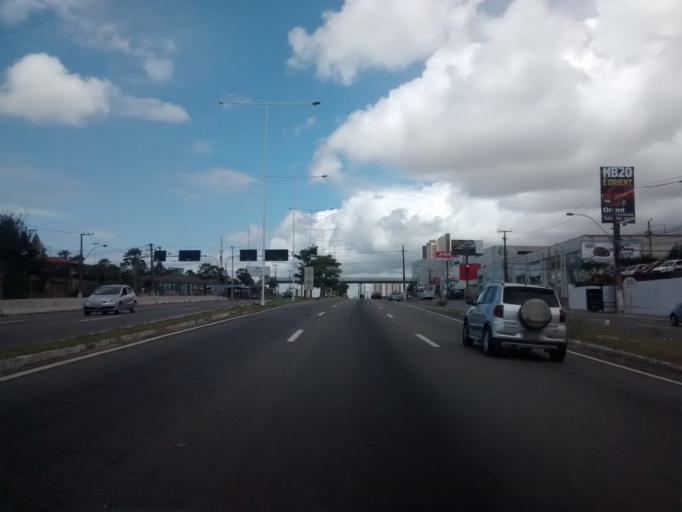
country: BR
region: Rio Grande do Norte
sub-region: Natal
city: Natal
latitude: -5.8389
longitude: -35.2111
